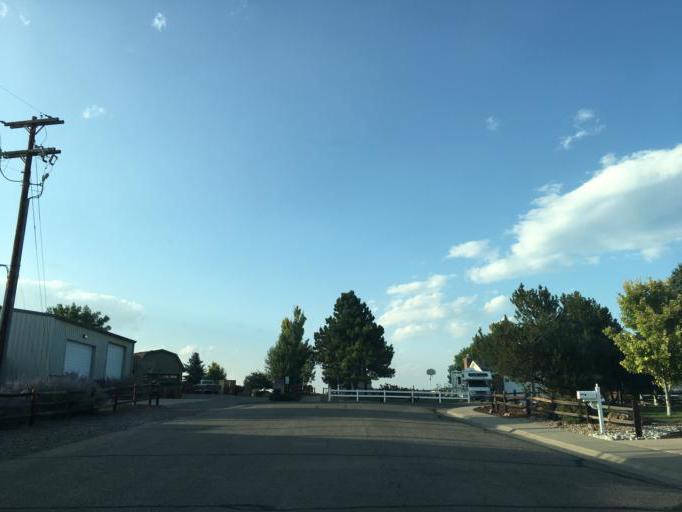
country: US
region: Colorado
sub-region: Jefferson County
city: Applewood
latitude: 39.7947
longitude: -105.1569
